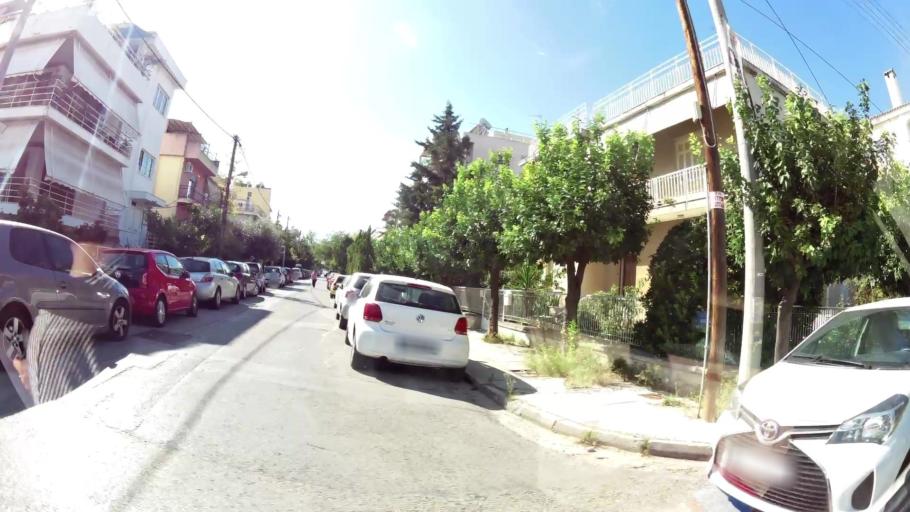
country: GR
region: Attica
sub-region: Nomarchia Athinas
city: Filothei
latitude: 38.0165
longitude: 23.7886
